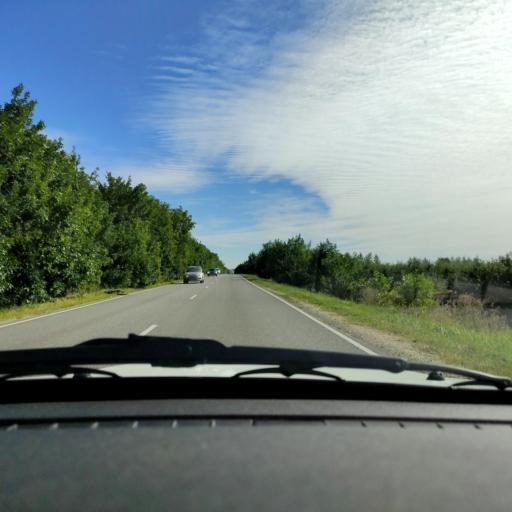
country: RU
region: Voronezj
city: Volya
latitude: 51.6953
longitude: 39.5050
